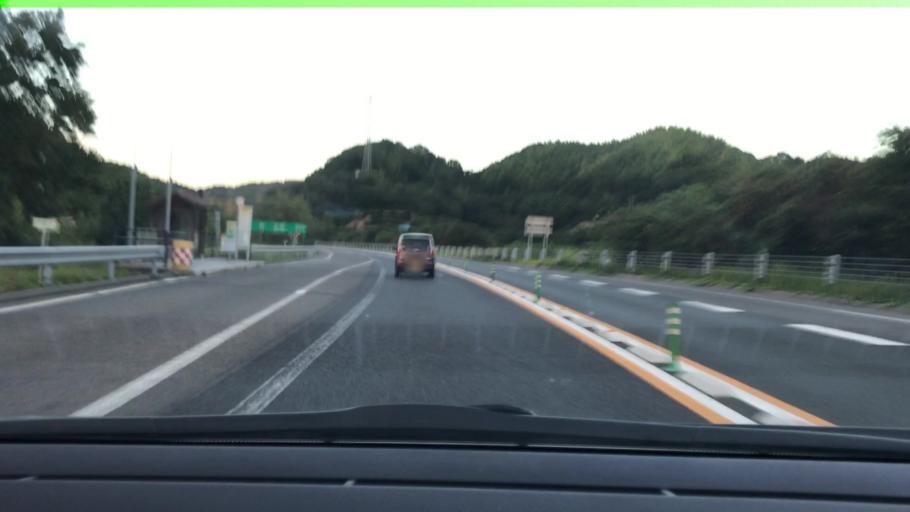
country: JP
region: Hiroshima
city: Innoshima
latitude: 34.3292
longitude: 133.1538
